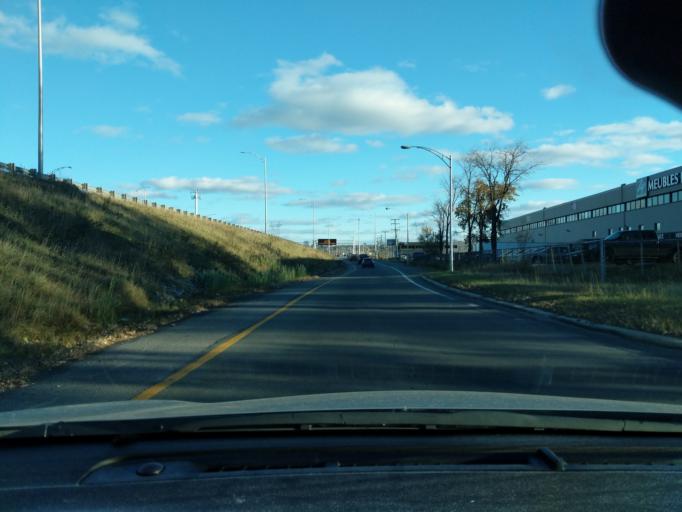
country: CA
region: Quebec
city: L'Ancienne-Lorette
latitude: 46.8036
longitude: -71.3286
